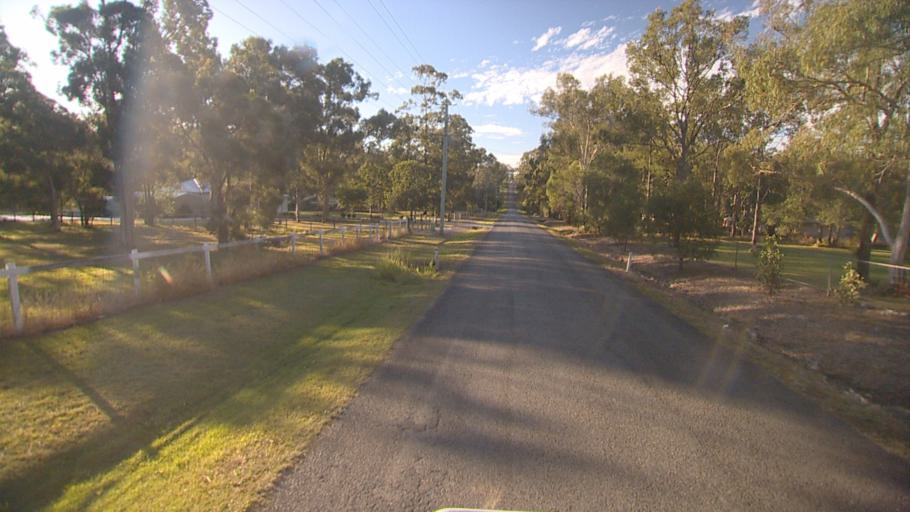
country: AU
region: Queensland
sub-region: Logan
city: Waterford West
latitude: -27.7250
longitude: 153.1532
